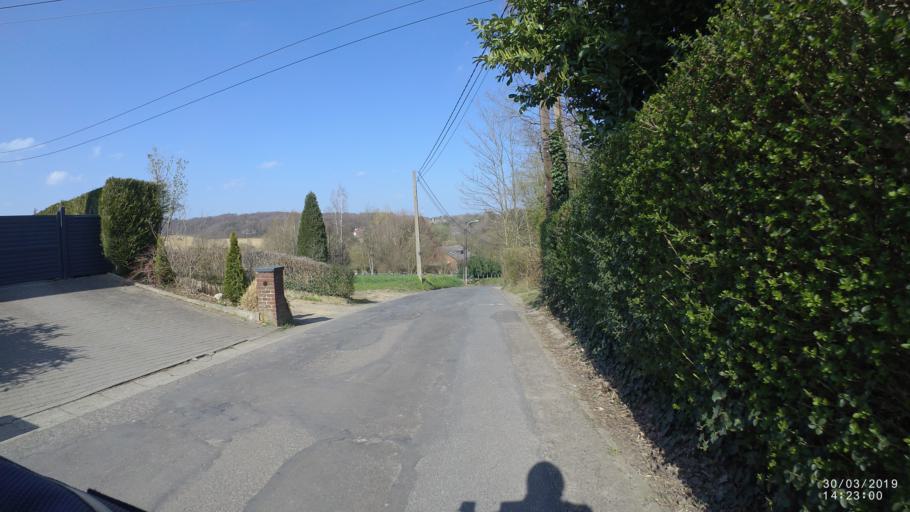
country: BE
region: Wallonia
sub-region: Province du Brabant Wallon
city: Wavre
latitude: 50.7060
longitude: 4.5757
